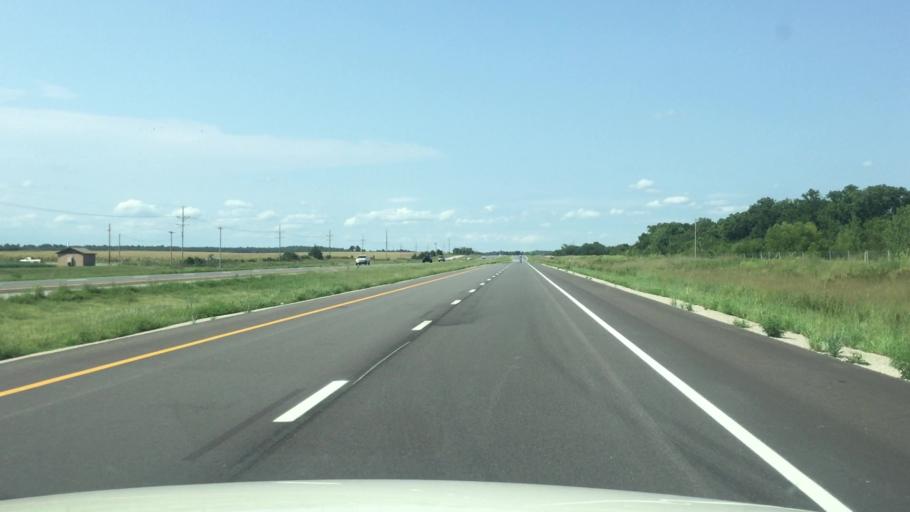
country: US
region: Kansas
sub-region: Linn County
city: La Cygne
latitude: 38.3143
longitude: -94.6774
